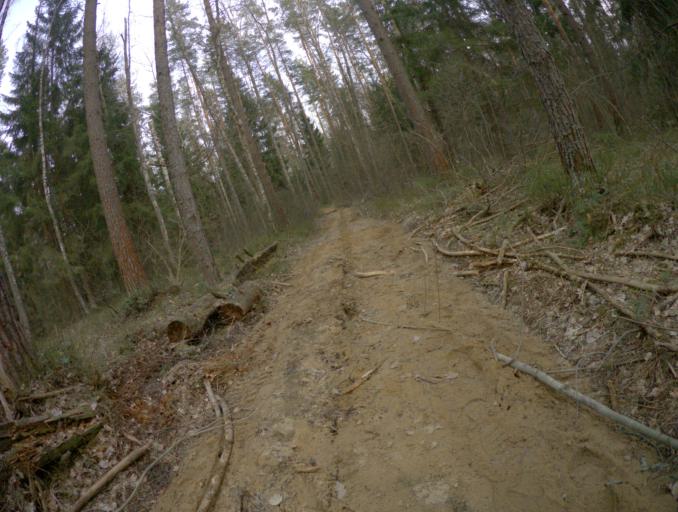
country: RU
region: Vladimir
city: Kommunar
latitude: 56.0807
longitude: 40.5073
